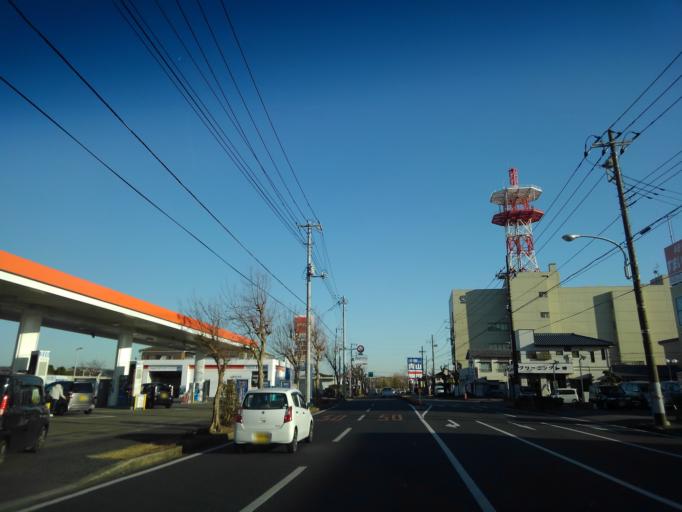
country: JP
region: Chiba
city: Kimitsu
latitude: 35.3271
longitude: 139.9059
